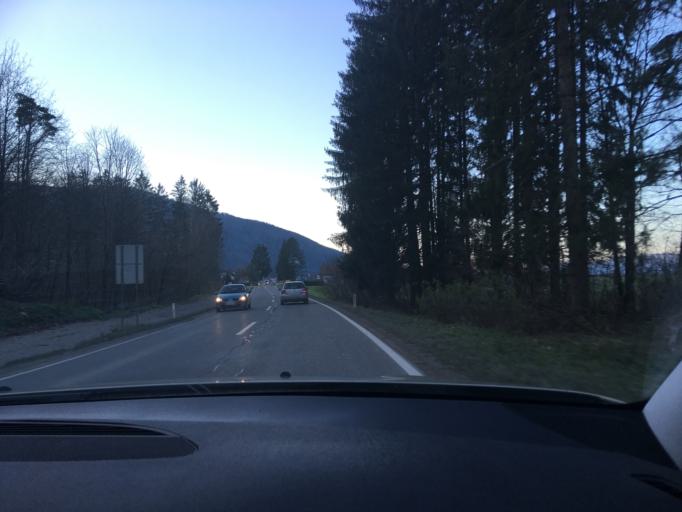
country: SI
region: Kocevje
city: Kocevje
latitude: 45.6560
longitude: 14.8468
